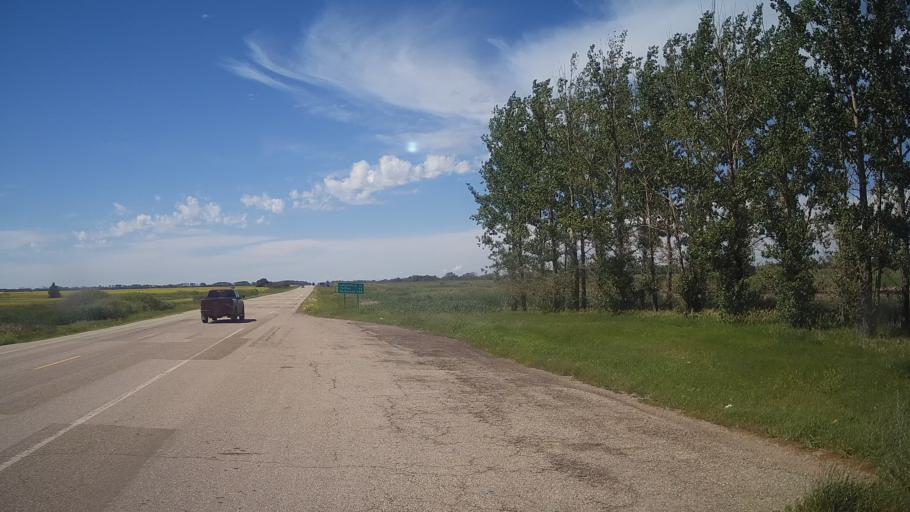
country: CA
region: Saskatchewan
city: Langenburg
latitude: 50.7784
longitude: -101.5121
